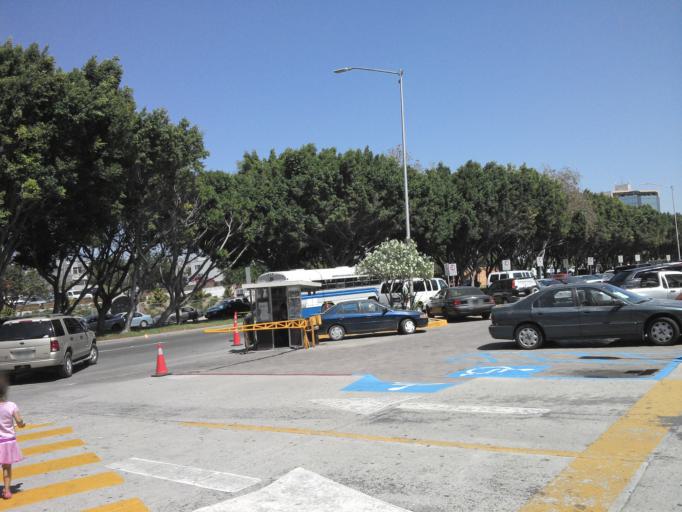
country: MX
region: Baja California
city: Tijuana
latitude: 32.5325
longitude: -117.0183
